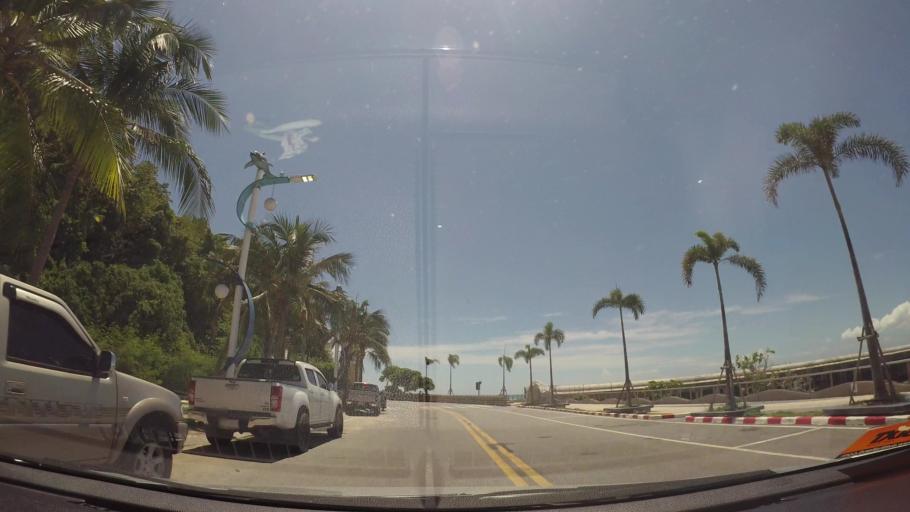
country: TH
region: Chon Buri
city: Phatthaya
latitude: 12.9298
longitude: 100.8627
